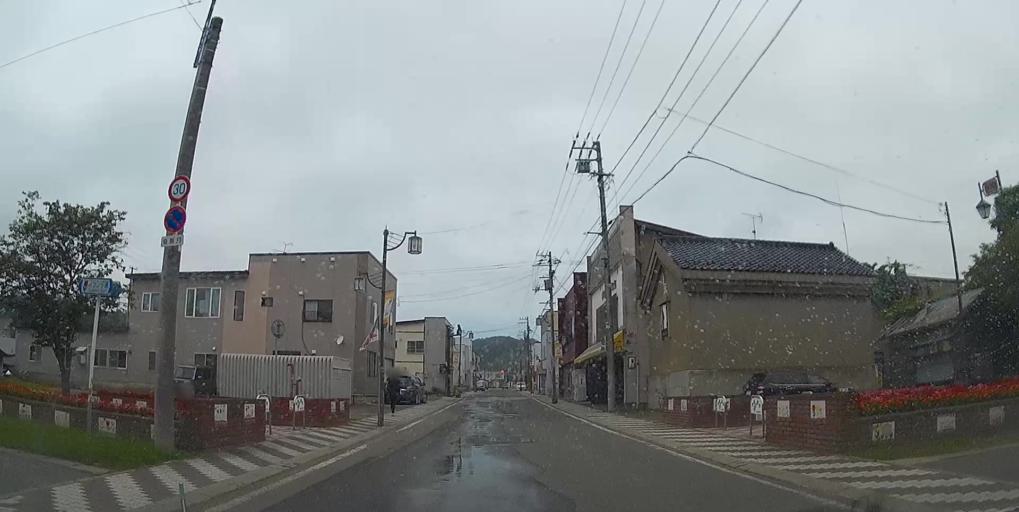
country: JP
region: Hokkaido
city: Iwanai
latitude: 42.4271
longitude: 140.0104
